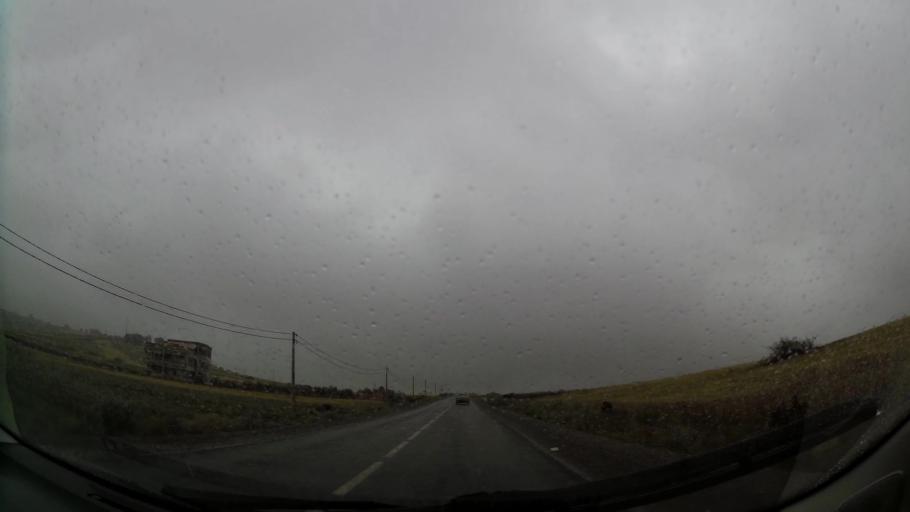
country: MA
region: Oriental
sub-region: Nador
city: Boudinar
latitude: 35.1366
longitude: -3.6219
